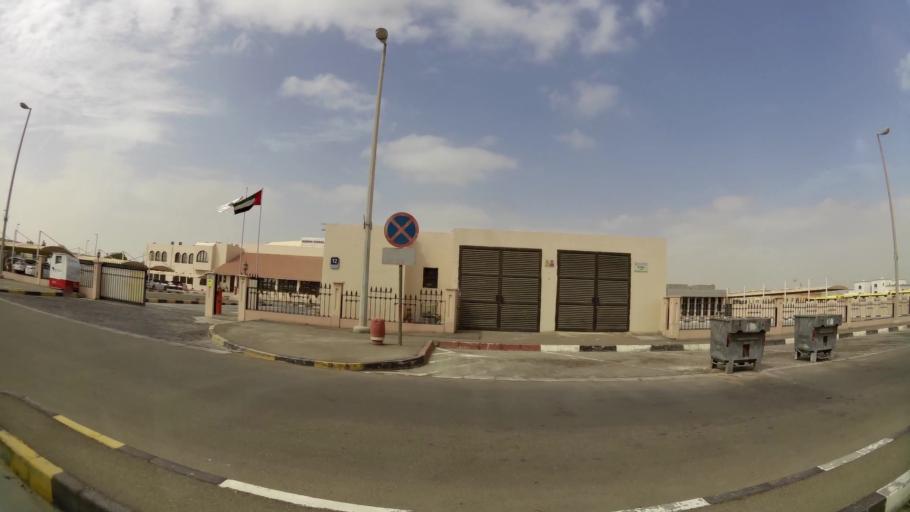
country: AE
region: Abu Dhabi
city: Abu Dhabi
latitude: 24.3935
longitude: 54.4979
